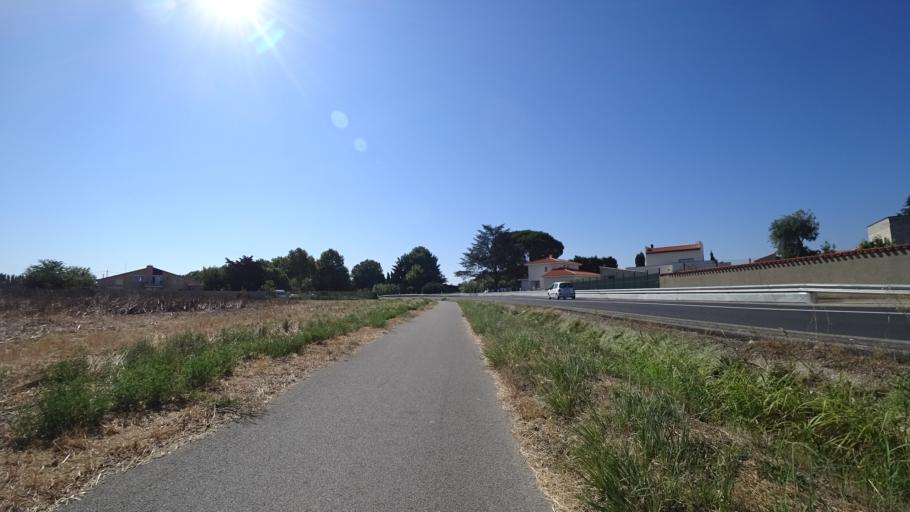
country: FR
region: Languedoc-Roussillon
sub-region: Departement des Pyrenees-Orientales
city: Bompas
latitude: 42.7260
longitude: 2.9474
